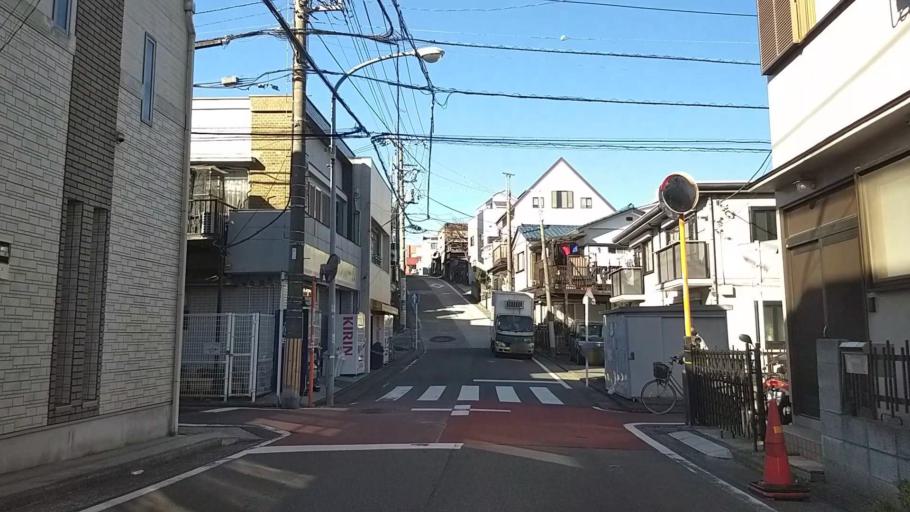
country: JP
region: Kanagawa
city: Yokohama
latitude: 35.4494
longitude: 139.6179
